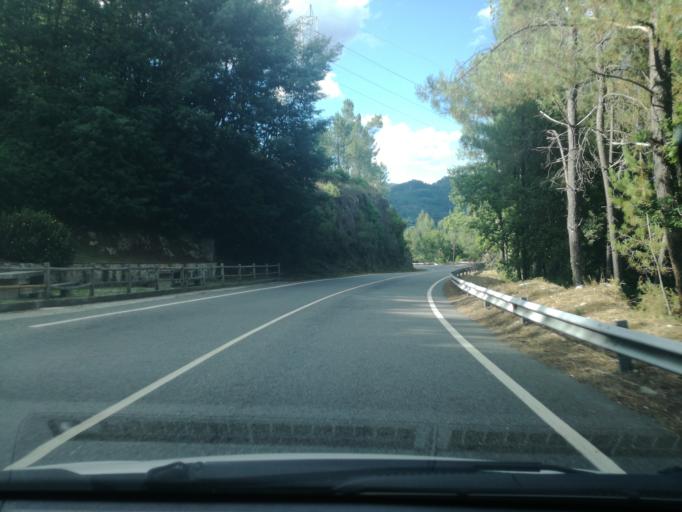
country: ES
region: Galicia
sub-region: Provincia de Ourense
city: Lobios
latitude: 41.9052
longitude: -8.0877
